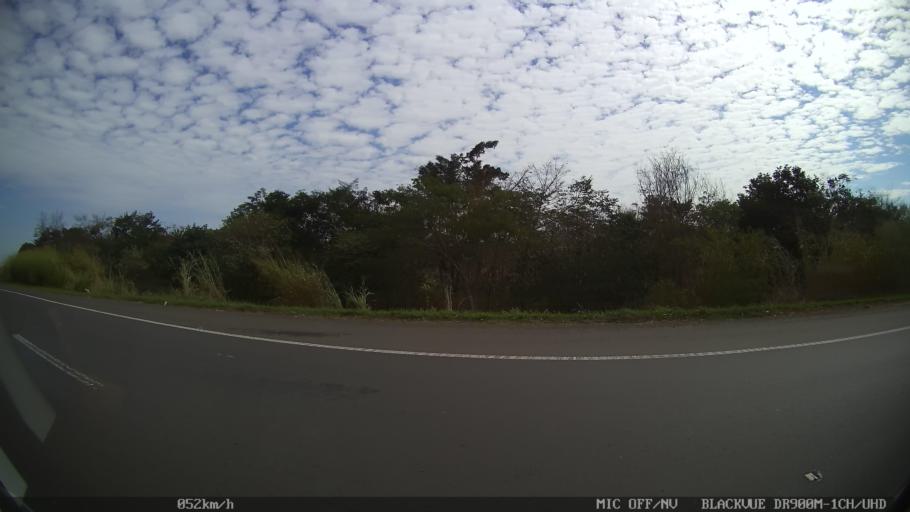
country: BR
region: Sao Paulo
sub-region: Santa Barbara D'Oeste
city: Santa Barbara d'Oeste
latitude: -22.7718
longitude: -47.4230
